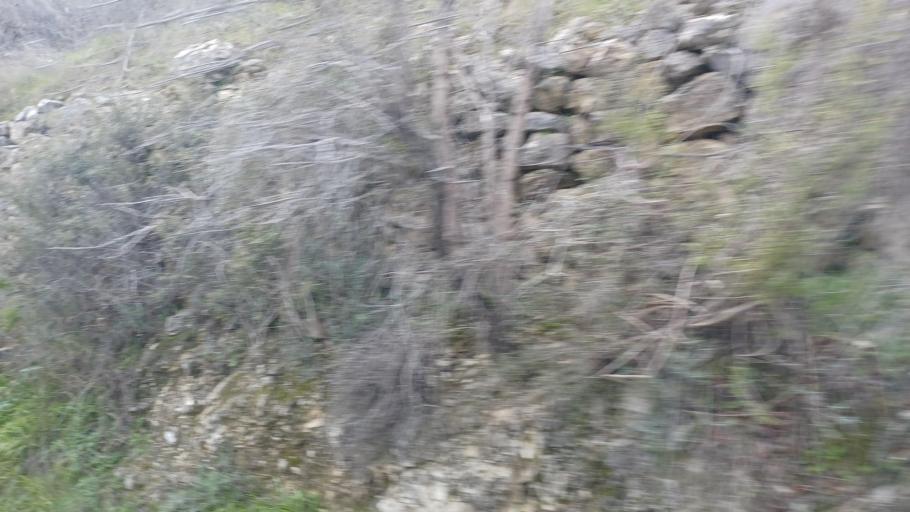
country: CY
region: Limassol
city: Pachna
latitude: 34.8578
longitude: 32.7106
